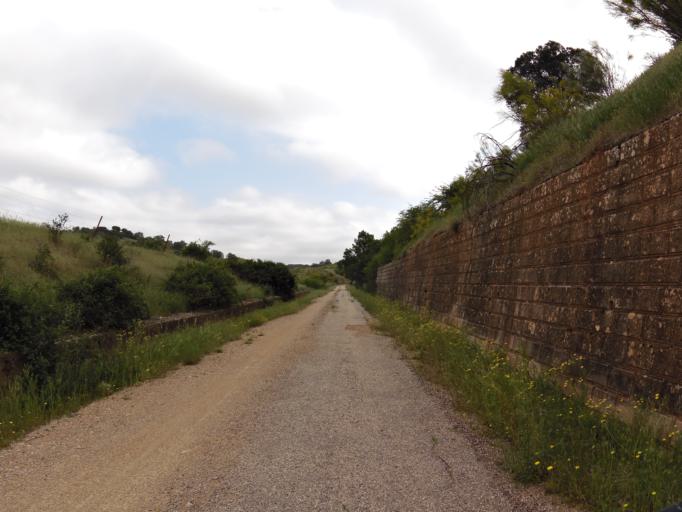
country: ES
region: Castille-La Mancha
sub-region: Provincia de Albacete
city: Alcaraz
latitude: 38.7078
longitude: -2.4999
